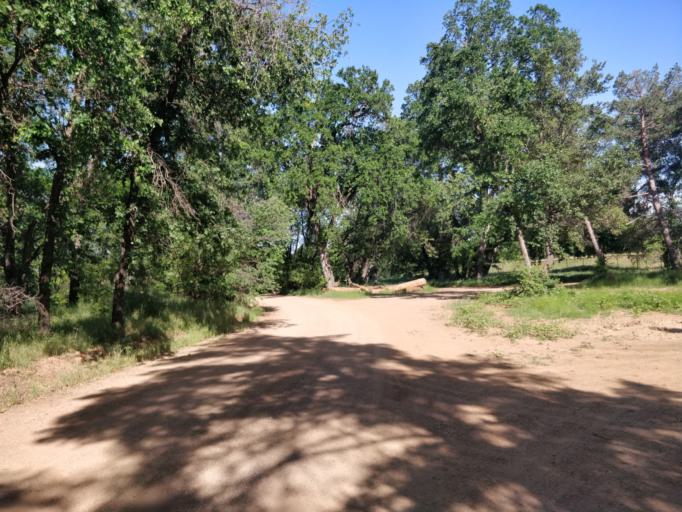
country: US
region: California
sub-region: Shasta County
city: Shasta Lake
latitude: 40.6305
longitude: -122.3114
